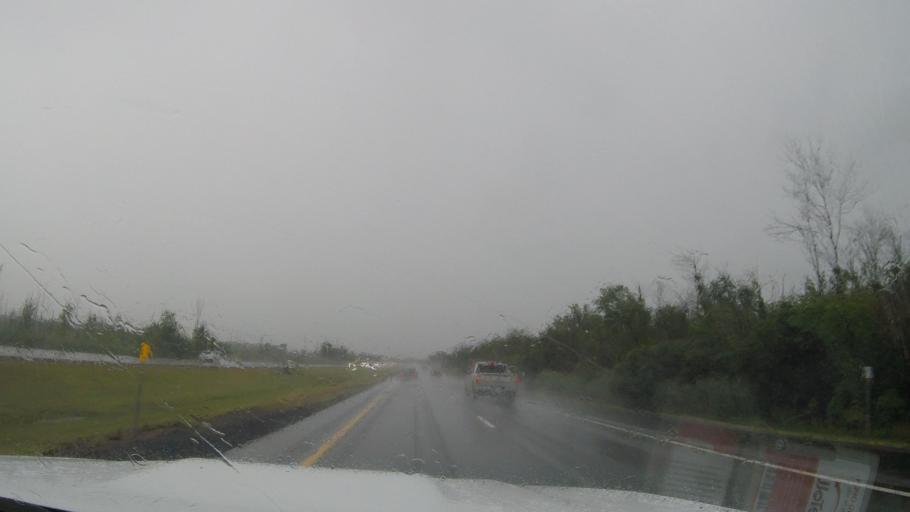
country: US
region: New York
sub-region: Seneca County
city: Waterloo
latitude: 42.9617
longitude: -76.8927
